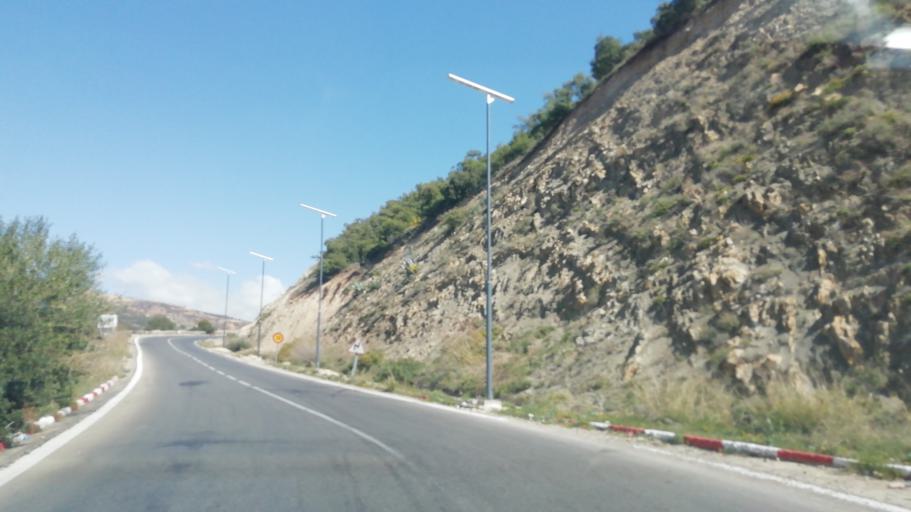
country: DZ
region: Mascara
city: Mascara
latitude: 35.5000
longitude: 0.1290
